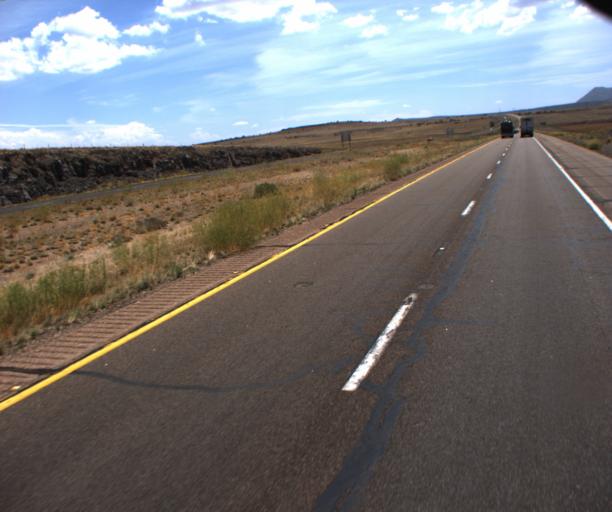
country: US
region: Arizona
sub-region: Yavapai County
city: Paulden
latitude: 35.3025
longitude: -112.8424
